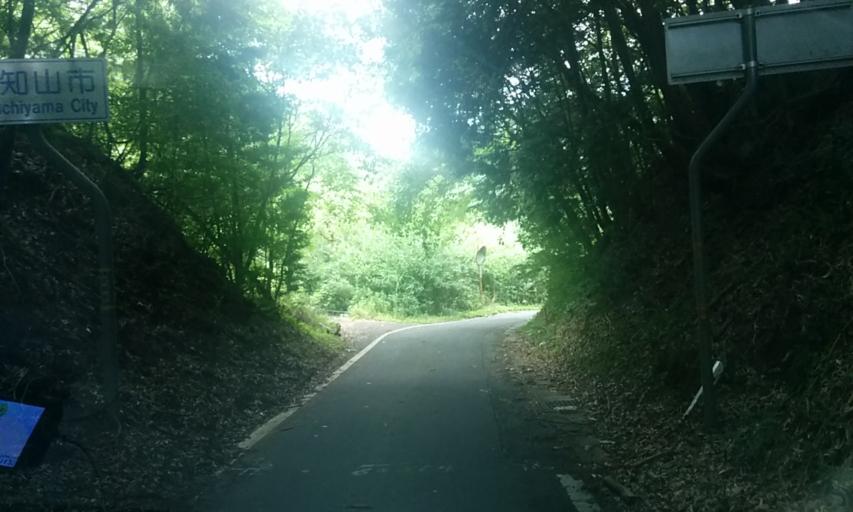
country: JP
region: Kyoto
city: Fukuchiyama
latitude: 35.3686
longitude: 135.1756
